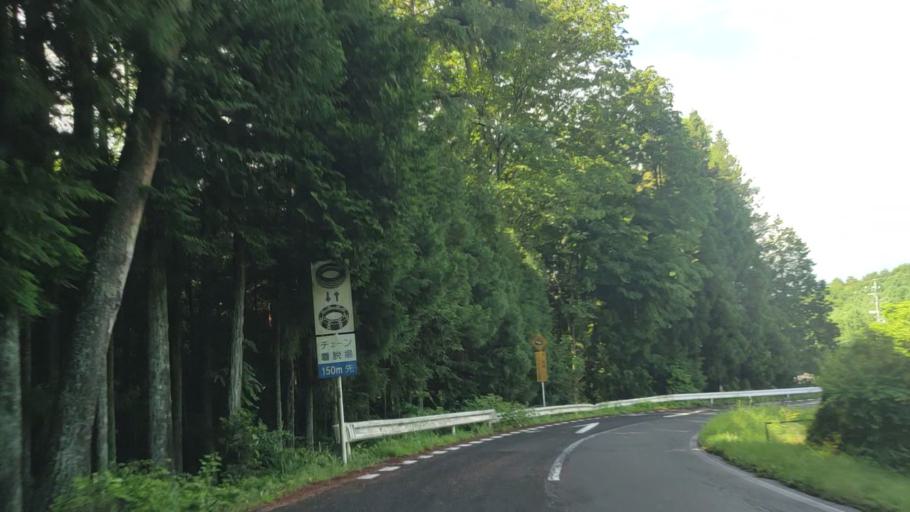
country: JP
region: Nagano
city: Suwa
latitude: 36.0708
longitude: 138.1358
